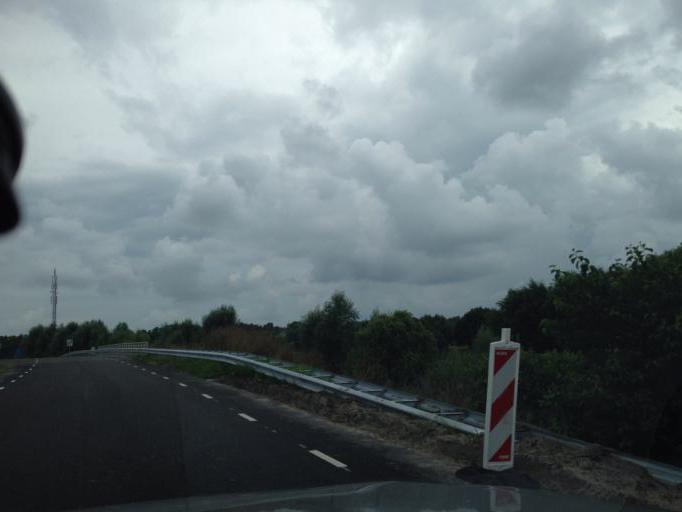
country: NL
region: Flevoland
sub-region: Gemeente Almere
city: Almere Stad
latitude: 52.3728
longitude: 5.2948
